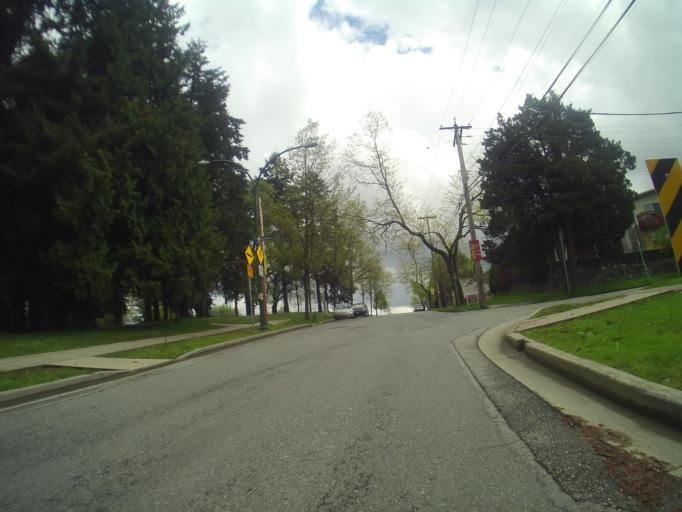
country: CA
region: British Columbia
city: Vancouver
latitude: 49.2565
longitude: -123.0731
